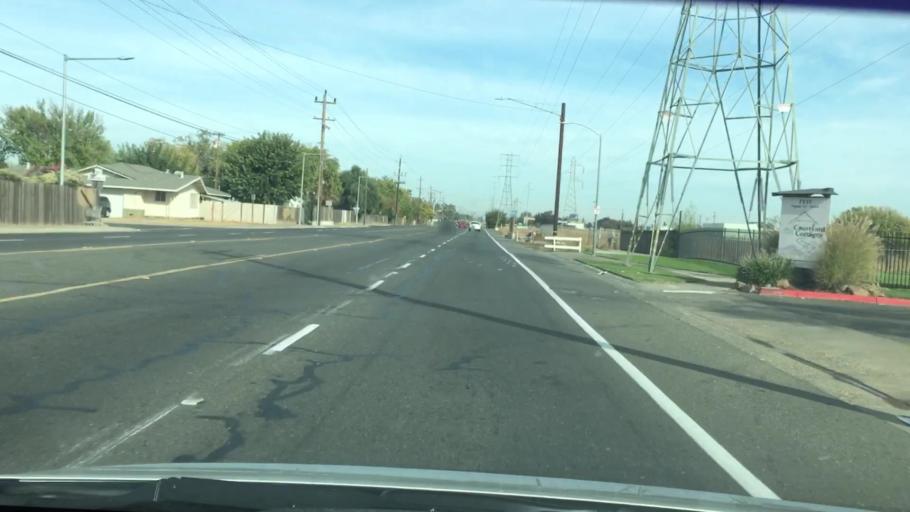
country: US
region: California
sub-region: Sacramento County
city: Florin
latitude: 38.4915
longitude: -121.4088
